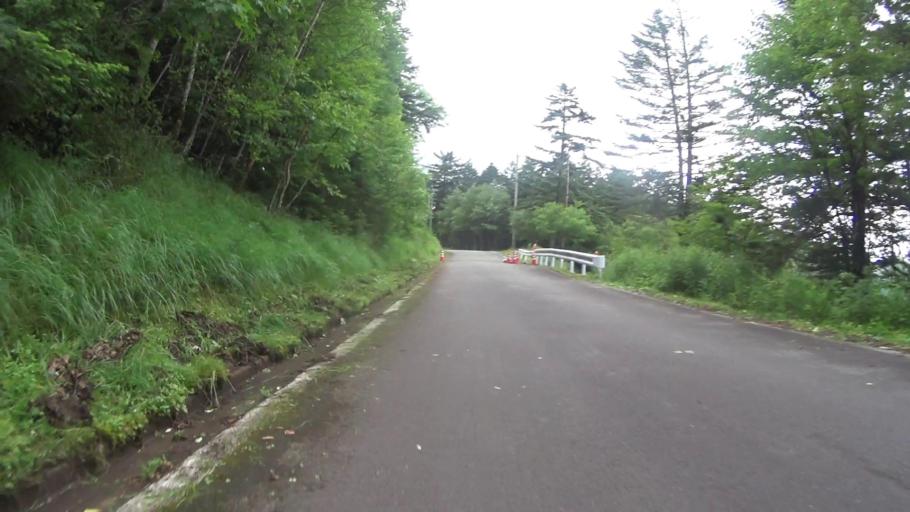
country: JP
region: Nagano
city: Saku
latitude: 36.1136
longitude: 138.3235
